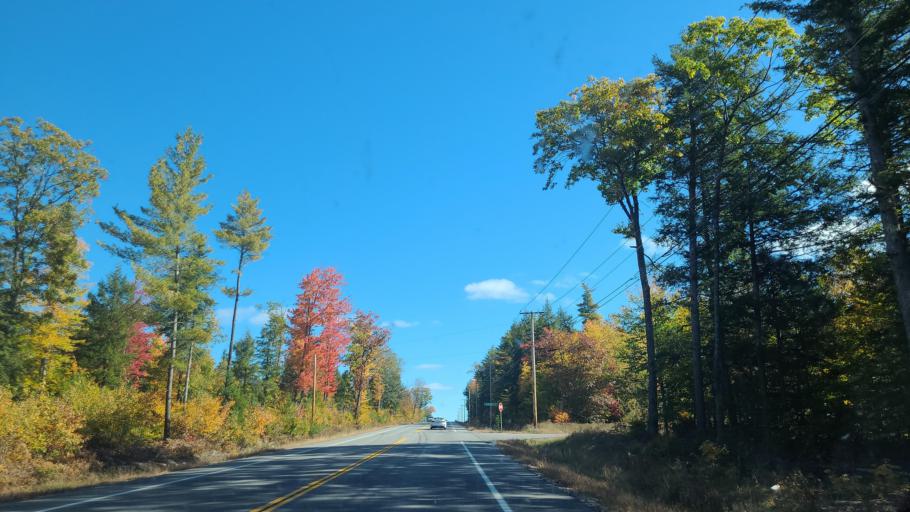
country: US
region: Maine
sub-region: Oxford County
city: Fryeburg
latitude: 44.0261
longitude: -70.9328
